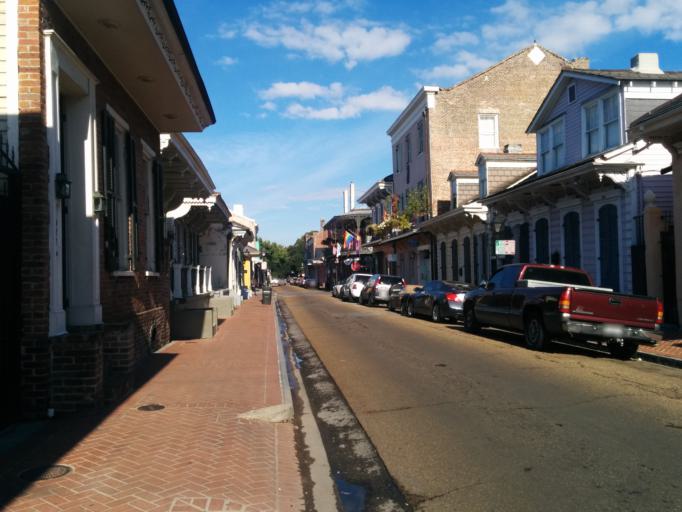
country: US
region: Louisiana
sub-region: Orleans Parish
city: New Orleans
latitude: 29.9595
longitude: -90.0670
